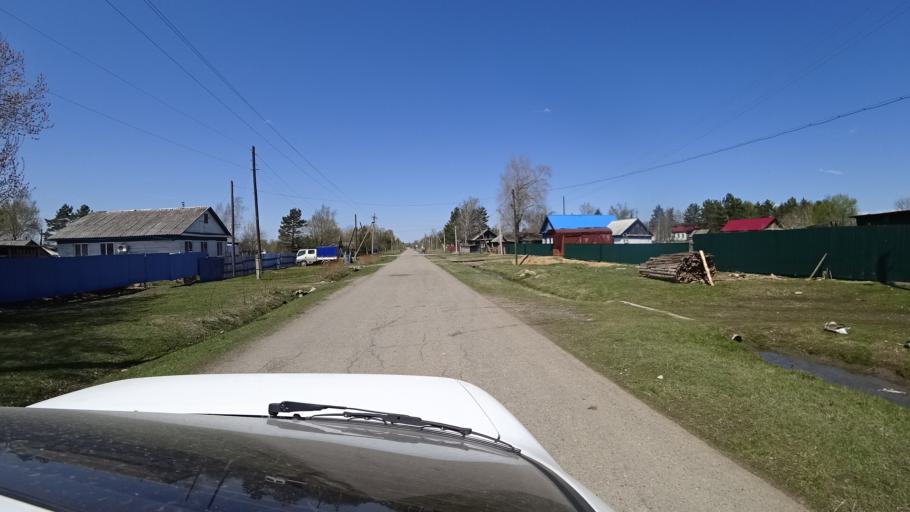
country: RU
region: Primorskiy
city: Lazo
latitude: 45.7932
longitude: 133.7666
